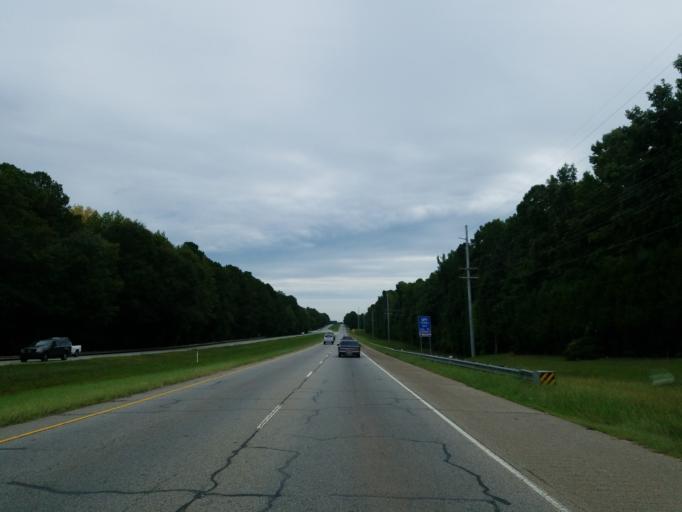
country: US
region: Georgia
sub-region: Spalding County
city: Griffin
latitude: 33.1935
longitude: -84.2814
